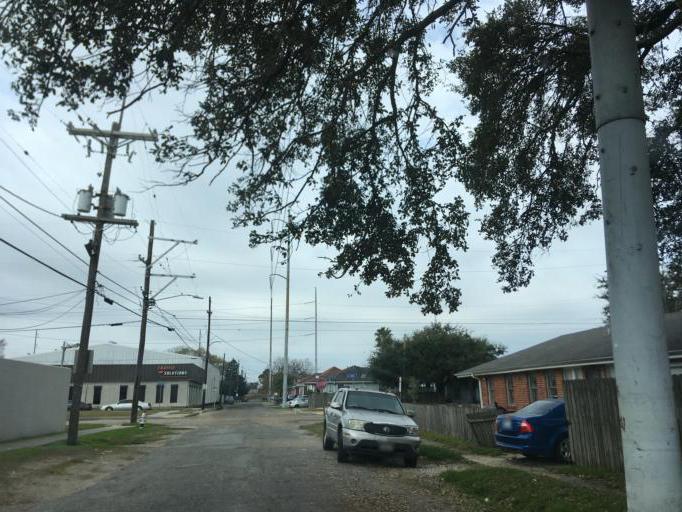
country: US
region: Louisiana
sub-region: Orleans Parish
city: New Orleans
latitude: 29.9884
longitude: -90.0629
